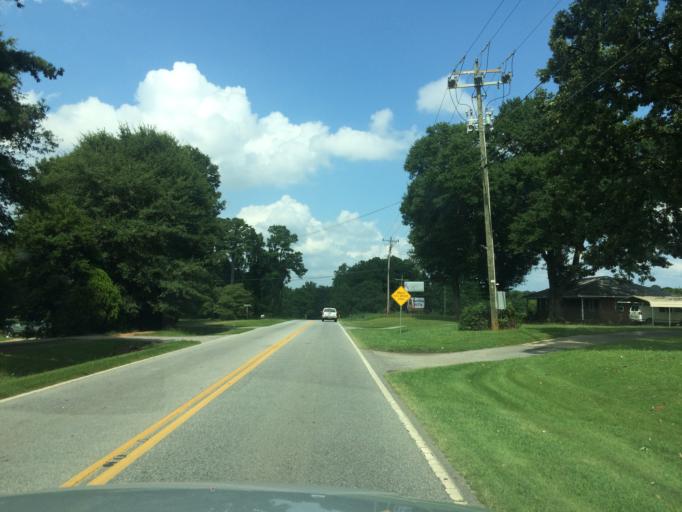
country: US
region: South Carolina
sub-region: Spartanburg County
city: Fairforest
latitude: 34.9594
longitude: -82.0065
